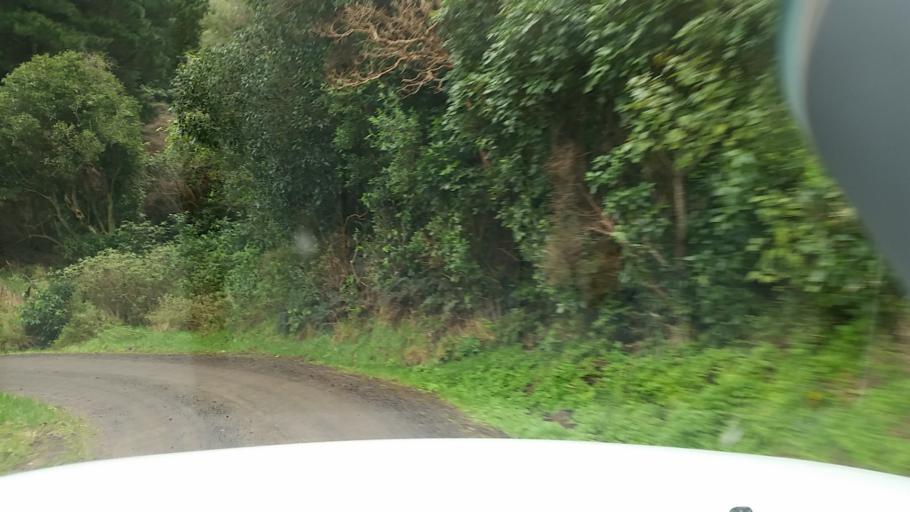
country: NZ
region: Canterbury
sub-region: Christchurch City
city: Christchurch
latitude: -43.6921
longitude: 172.7860
